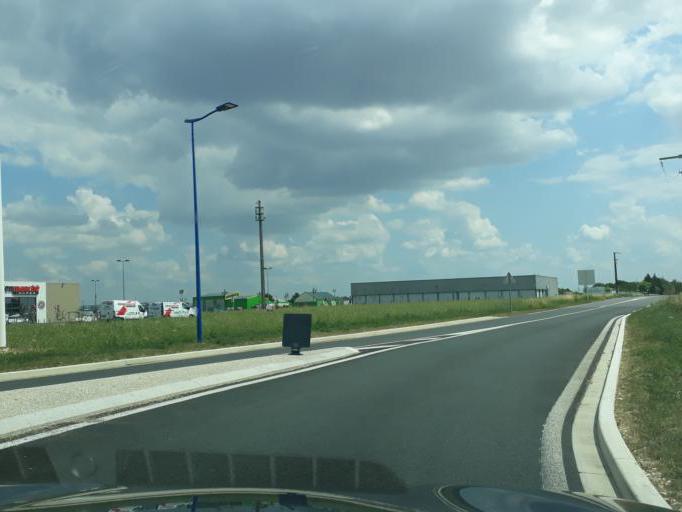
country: FR
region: Centre
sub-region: Departement du Cher
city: Avord
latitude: 47.0322
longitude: 2.6412
